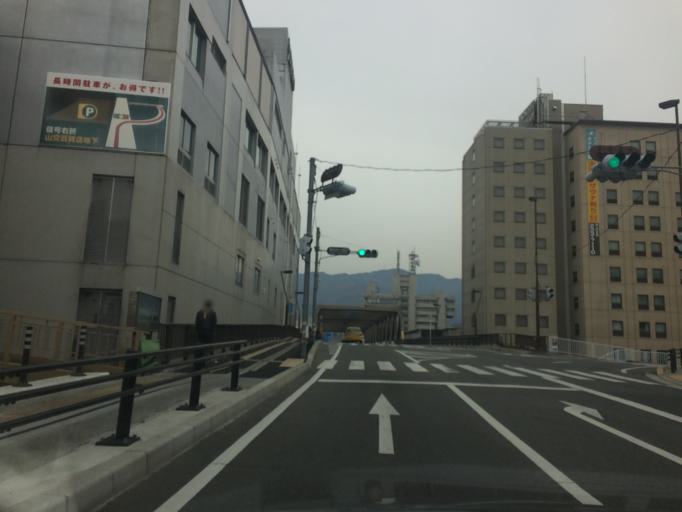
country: JP
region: Yamanashi
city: Kofu-shi
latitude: 35.6653
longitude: 138.5697
